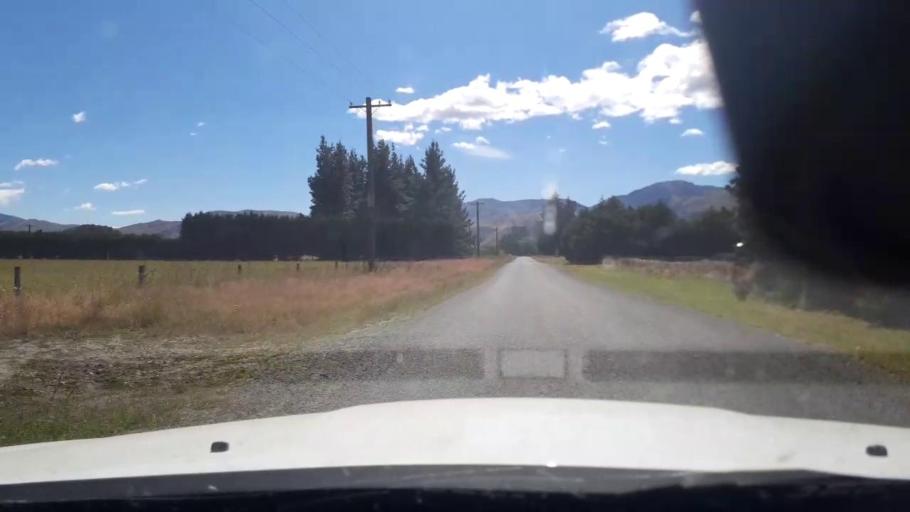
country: NZ
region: Canterbury
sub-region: Timaru District
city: Pleasant Point
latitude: -44.0012
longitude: 170.8408
